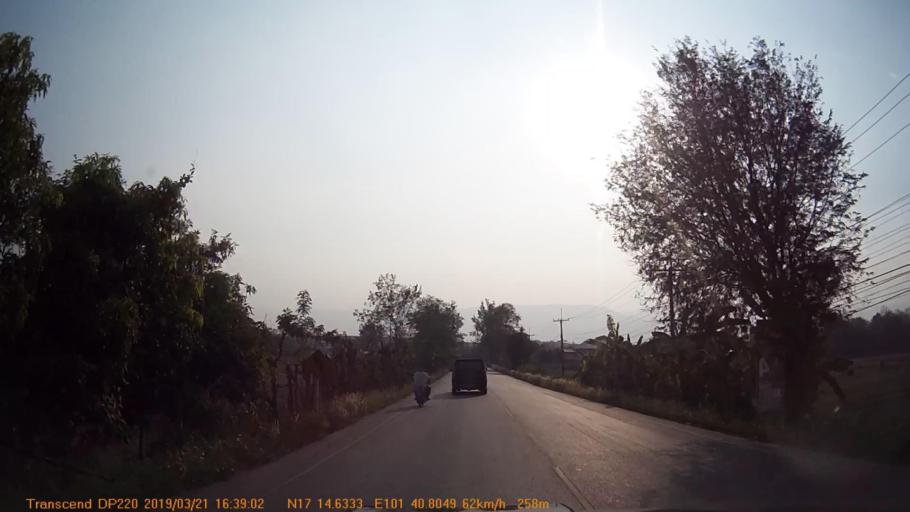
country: TH
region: Loei
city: Wang Saphung
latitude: 17.2439
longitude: 101.6800
